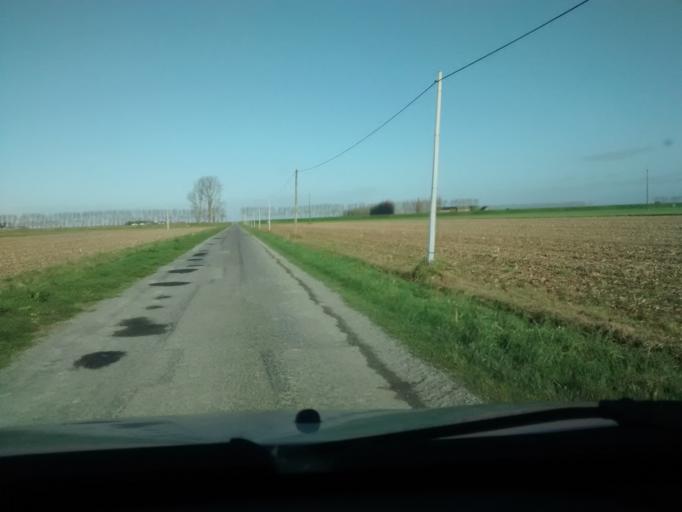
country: FR
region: Brittany
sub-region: Departement d'Ille-et-Vilaine
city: Roz-sur-Couesnon
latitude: 48.6049
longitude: -1.5821
